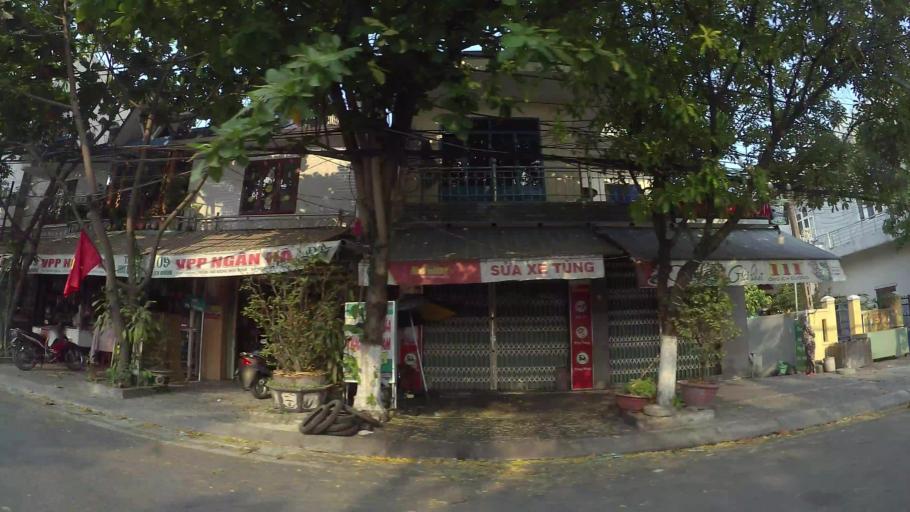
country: VN
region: Da Nang
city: Cam Le
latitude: 16.0191
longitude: 108.2037
